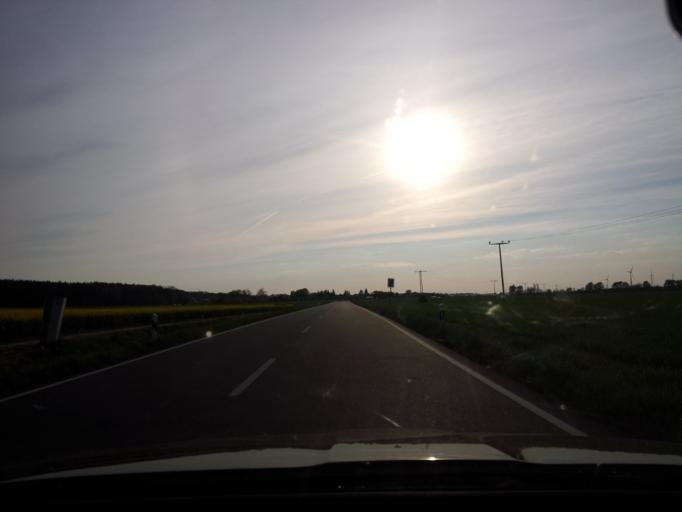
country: DE
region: Brandenburg
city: Drahnsdorf
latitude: 51.8492
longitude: 13.5468
